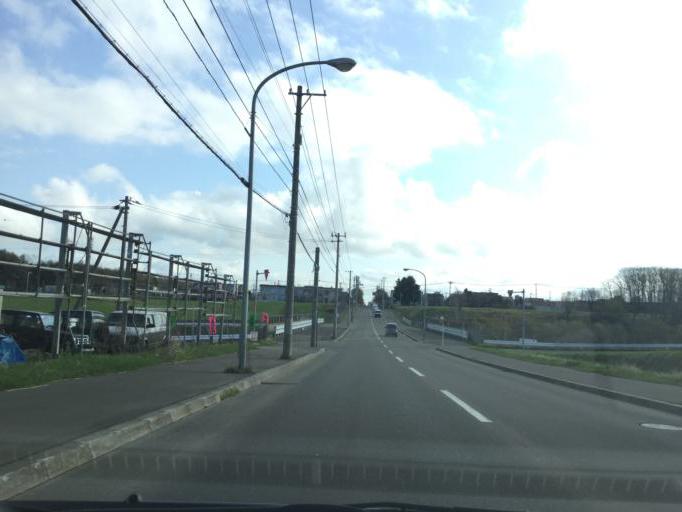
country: JP
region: Hokkaido
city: Ebetsu
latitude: 43.0914
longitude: 141.5016
